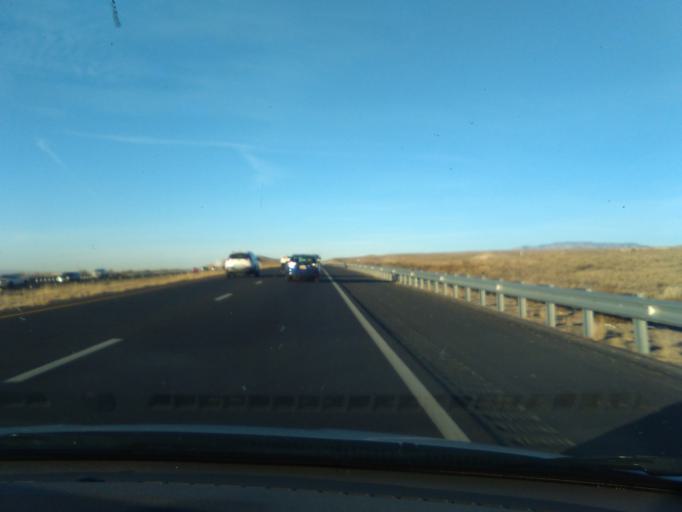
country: US
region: New Mexico
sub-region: Bernalillo County
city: South Valley
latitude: 34.9700
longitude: -106.6550
